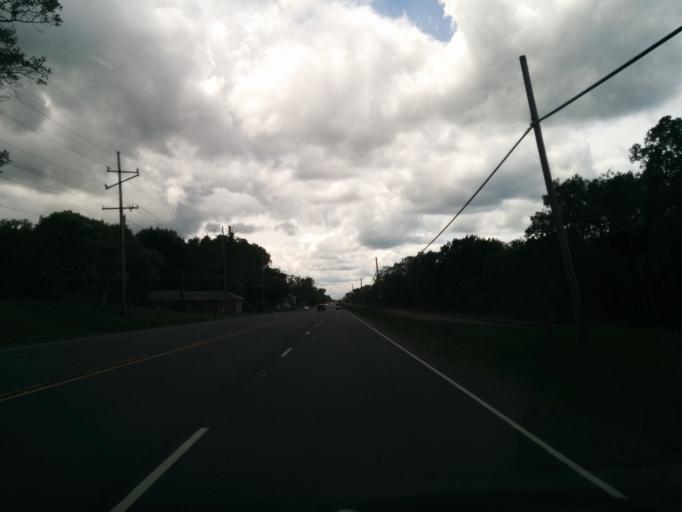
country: US
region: Indiana
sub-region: LaPorte County
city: Long Beach
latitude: 41.7386
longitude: -86.8438
